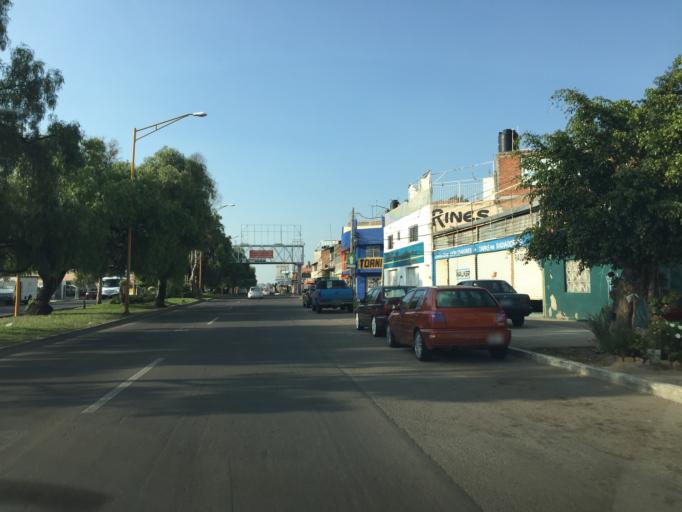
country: MX
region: Aguascalientes
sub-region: Aguascalientes
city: La Loma de los Negritos
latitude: 21.8636
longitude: -102.3173
